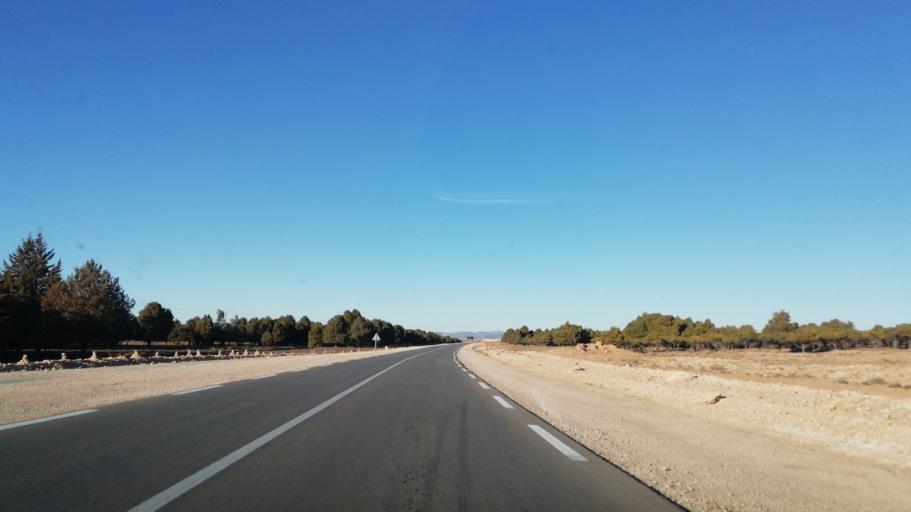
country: DZ
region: Tlemcen
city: Sebdou
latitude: 34.4597
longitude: -1.2754
